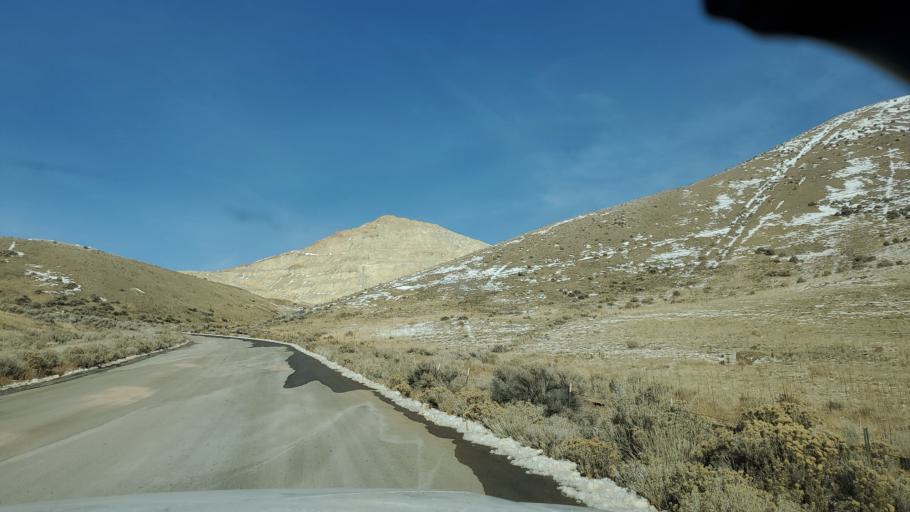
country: US
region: Utah
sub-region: Salt Lake County
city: Bluffdale
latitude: 40.4579
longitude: -111.8950
